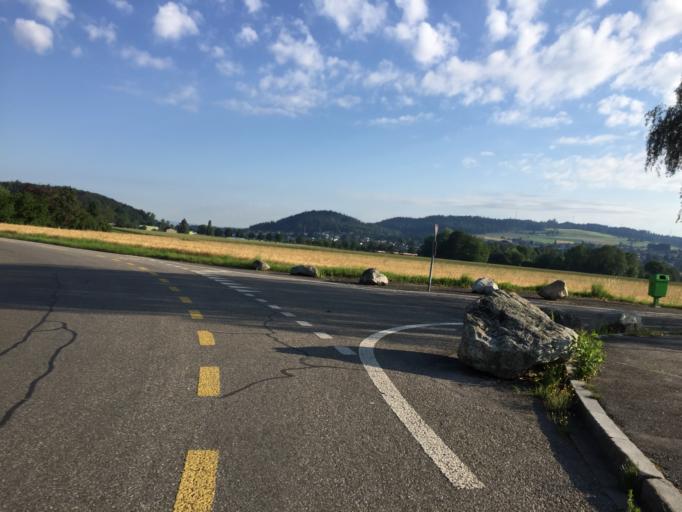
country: CH
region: Bern
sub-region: Bern-Mittelland District
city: Bolligen
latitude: 46.9612
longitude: 7.4919
